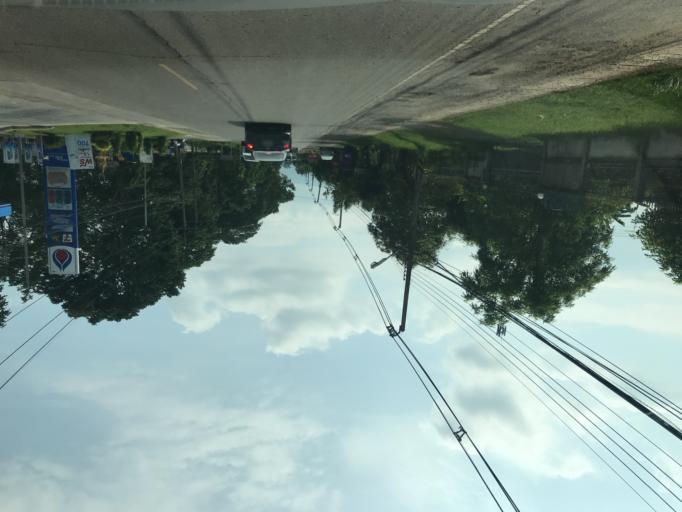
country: TH
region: Phayao
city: Chiang Kham
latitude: 19.5166
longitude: 100.3130
